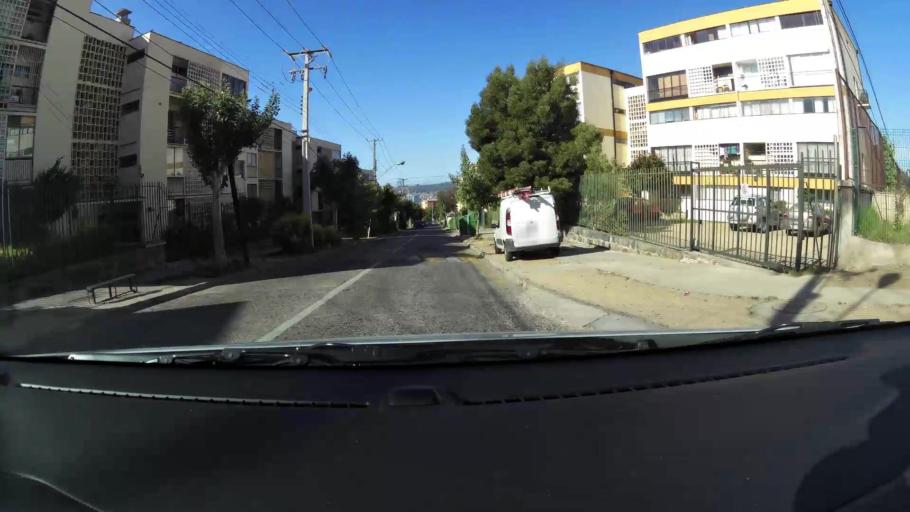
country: CL
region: Valparaiso
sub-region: Provincia de Valparaiso
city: Vina del Mar
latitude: -33.0315
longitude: -71.5578
